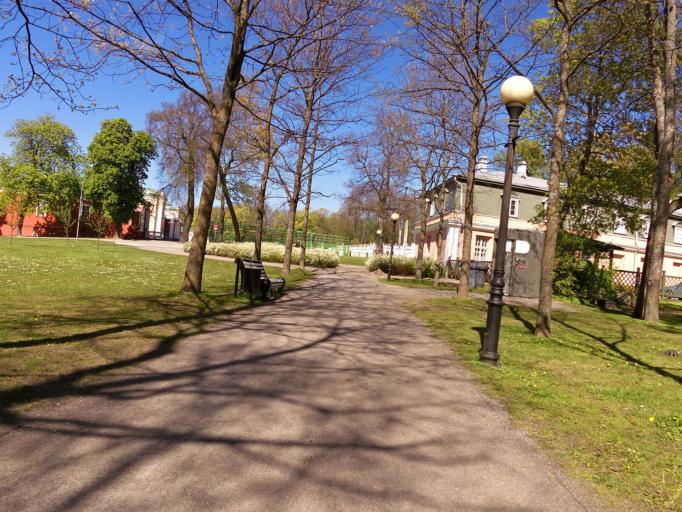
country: EE
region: Harju
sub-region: Tallinna linn
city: Tallinn
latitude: 59.4372
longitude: 24.7906
